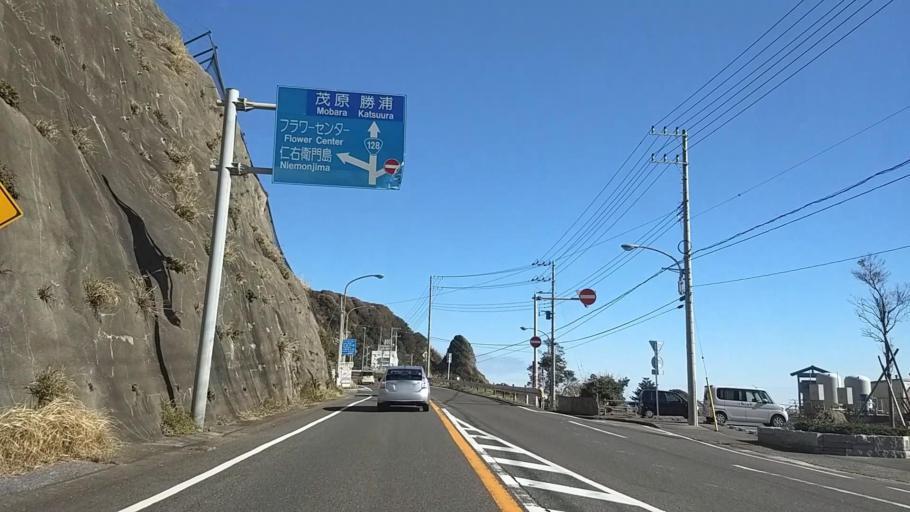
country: JP
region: Chiba
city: Kawaguchi
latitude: 35.0764
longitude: 140.0950
